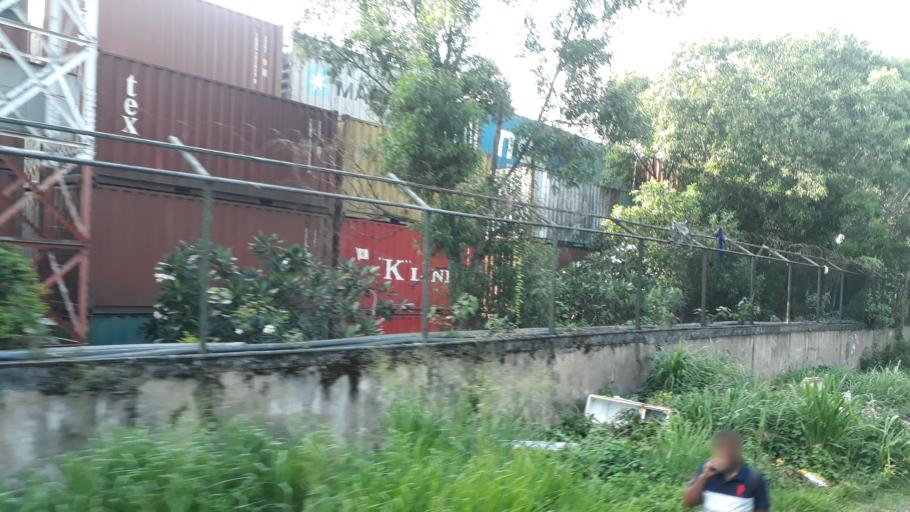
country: LK
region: Western
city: Kolonnawa
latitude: 6.9413
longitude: 79.8830
